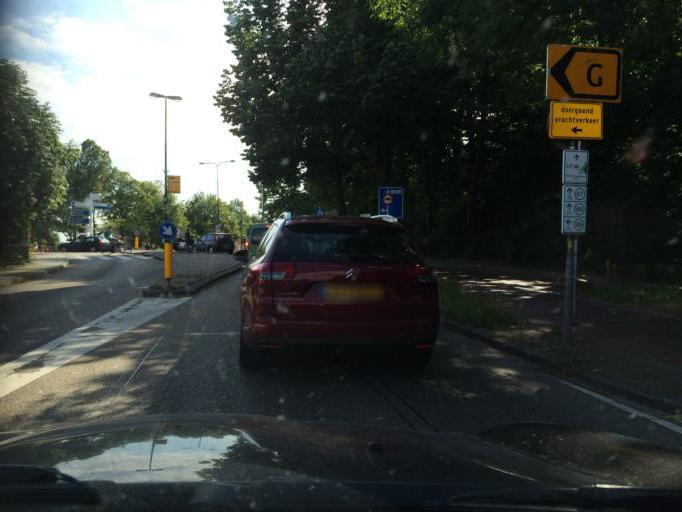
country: NL
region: Utrecht
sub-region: Gemeente Woerden
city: Woerden
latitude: 52.0875
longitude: 4.8913
